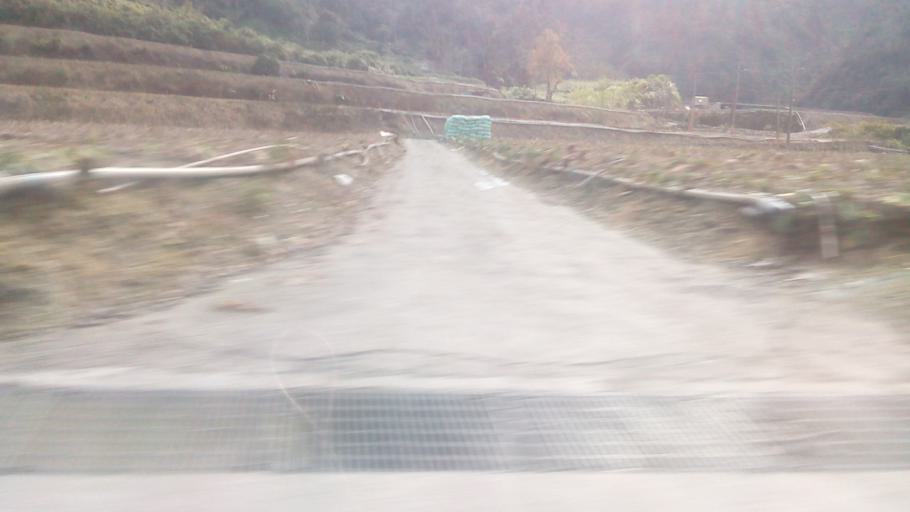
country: TW
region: Taiwan
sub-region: Yilan
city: Yilan
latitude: 24.5540
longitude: 121.4712
